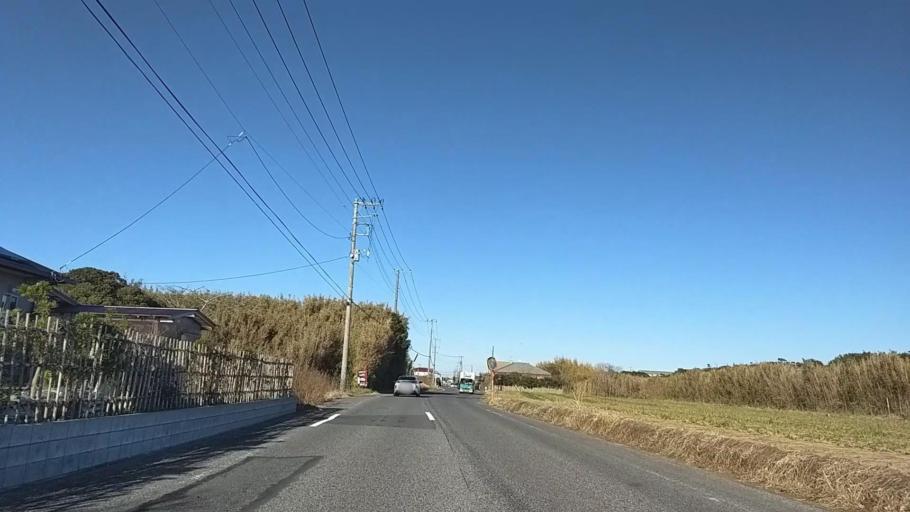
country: JP
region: Chiba
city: Mobara
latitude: 35.4052
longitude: 140.3878
